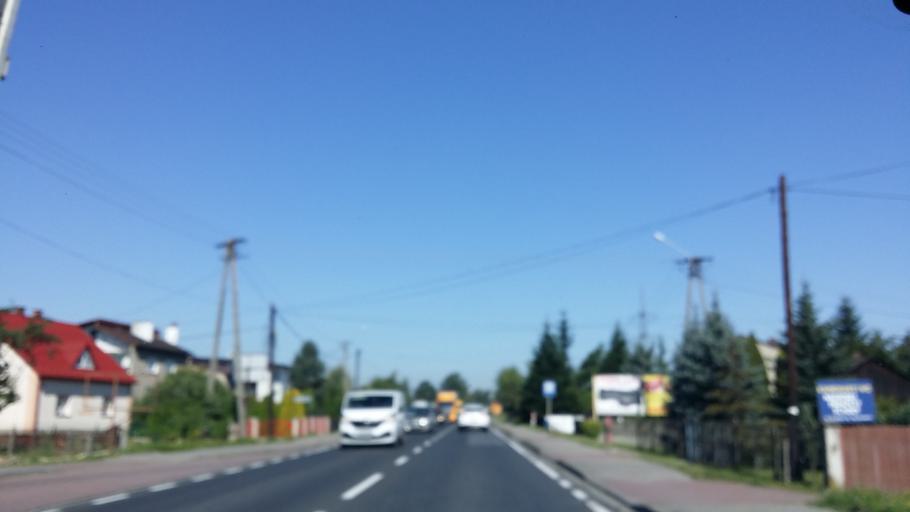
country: PL
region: Lesser Poland Voivodeship
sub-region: Powiat oswiecimski
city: Babice
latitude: 50.0561
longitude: 19.1990
